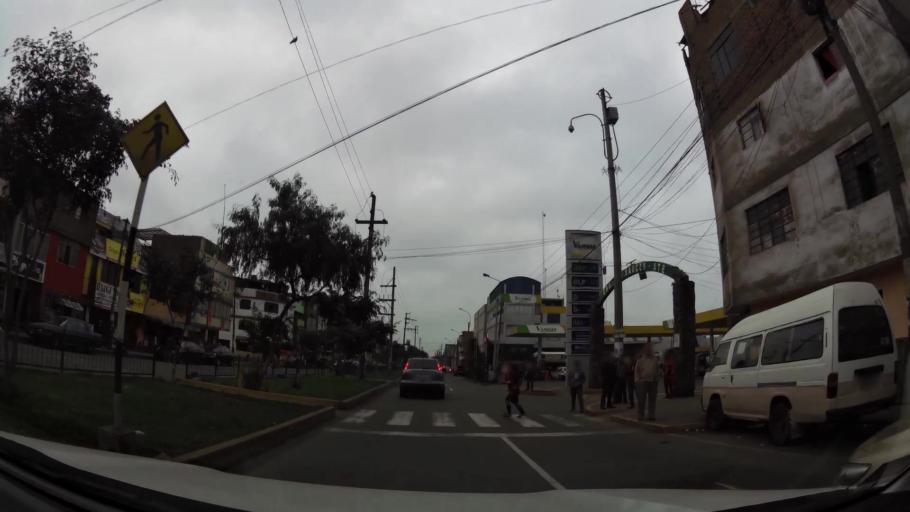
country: PE
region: Lima
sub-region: Lima
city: San Luis
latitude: -12.0688
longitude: -76.9803
